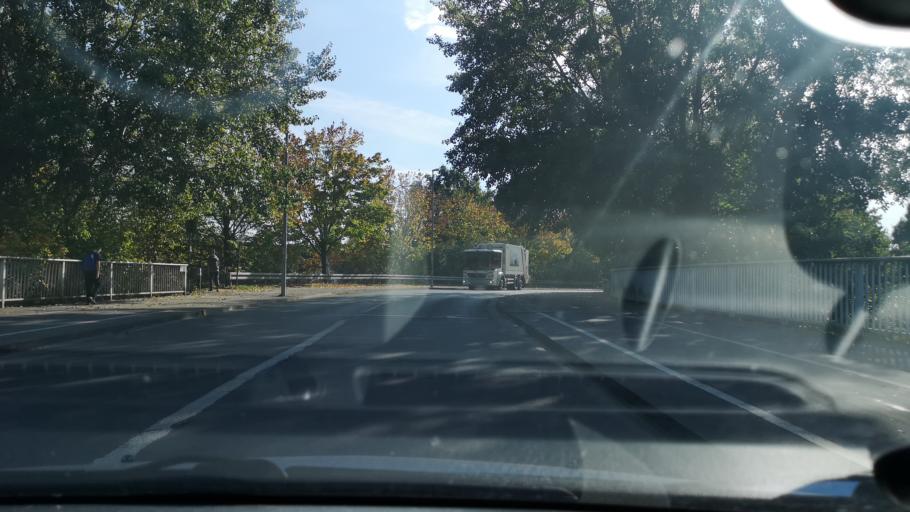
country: DE
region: Lower Saxony
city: Auf der Horst
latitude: 52.4141
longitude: 9.6112
